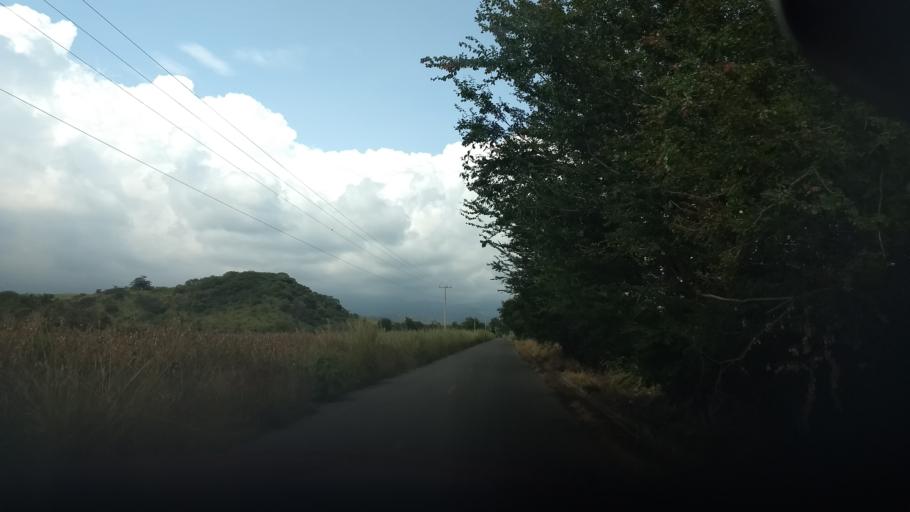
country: MX
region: Jalisco
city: Tonila
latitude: 19.4219
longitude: -103.4899
